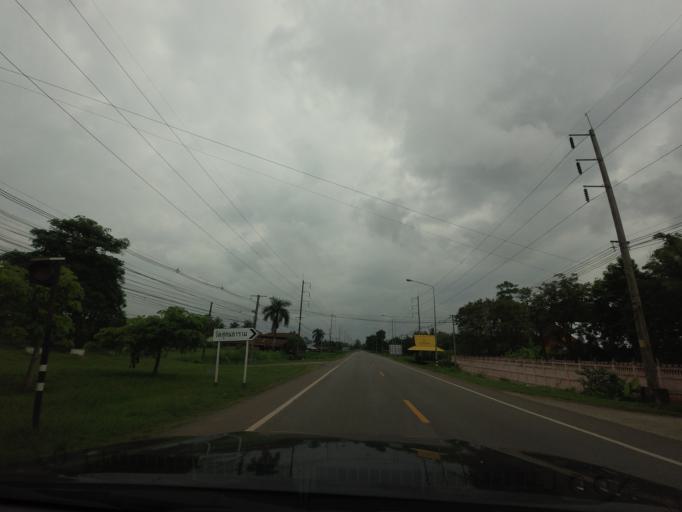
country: TH
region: Nong Khai
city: Tha Bo
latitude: 17.8998
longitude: 102.6039
